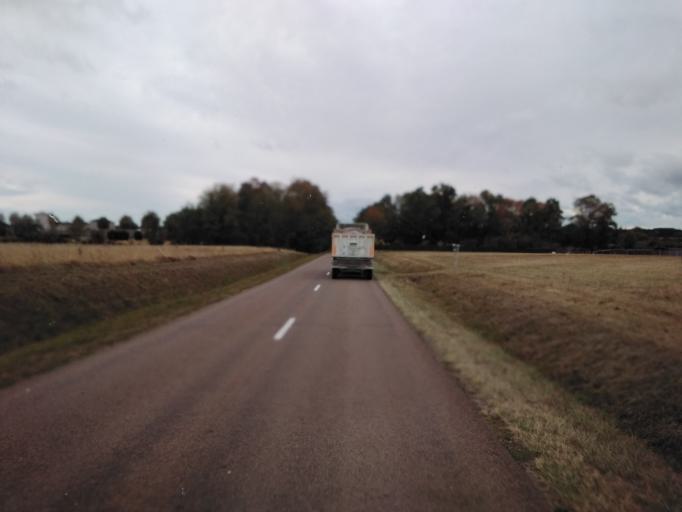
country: FR
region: Champagne-Ardenne
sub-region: Departement de l'Aube
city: Vendeuvre-sur-Barse
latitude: 48.2442
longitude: 4.4790
